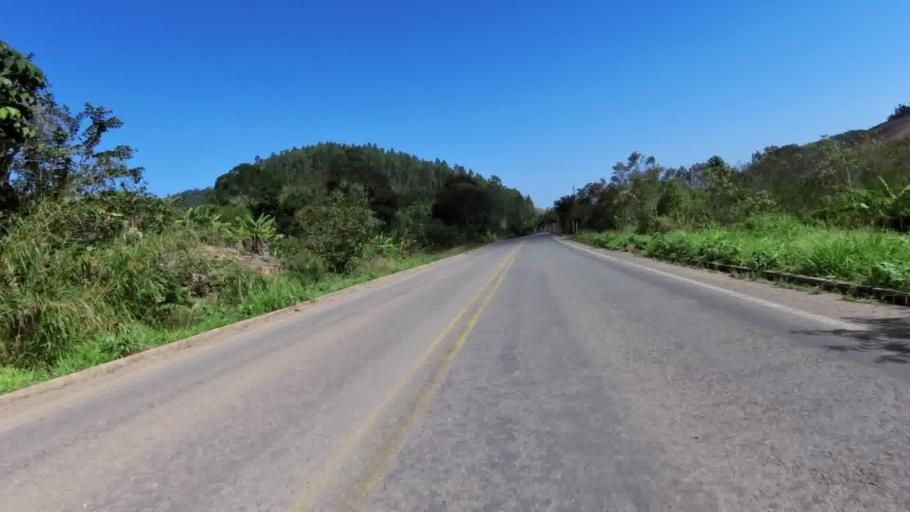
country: BR
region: Espirito Santo
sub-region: Alfredo Chaves
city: Alfredo Chaves
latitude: -20.5138
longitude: -40.7742
